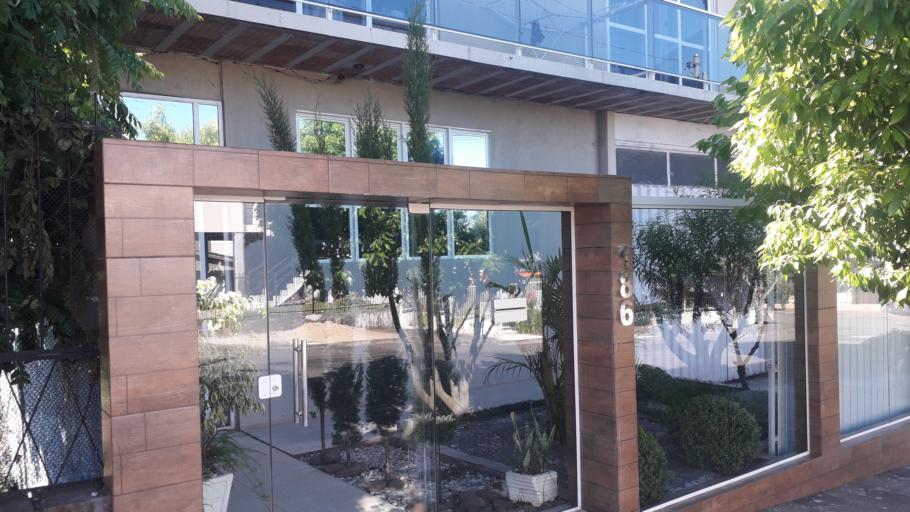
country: BR
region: Rio Grande do Sul
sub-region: Passo Fundo
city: Passo Fundo
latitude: -28.2648
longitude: -52.3757
